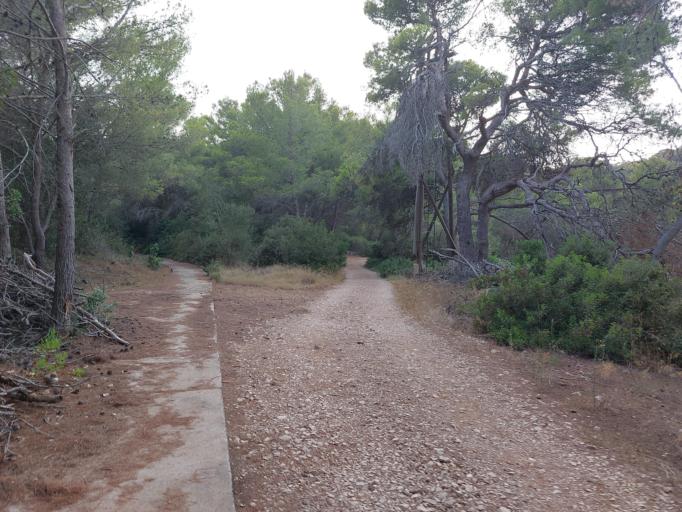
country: HR
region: Dubrovacko-Neretvanska
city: Smokvica
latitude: 42.7631
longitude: 16.8092
